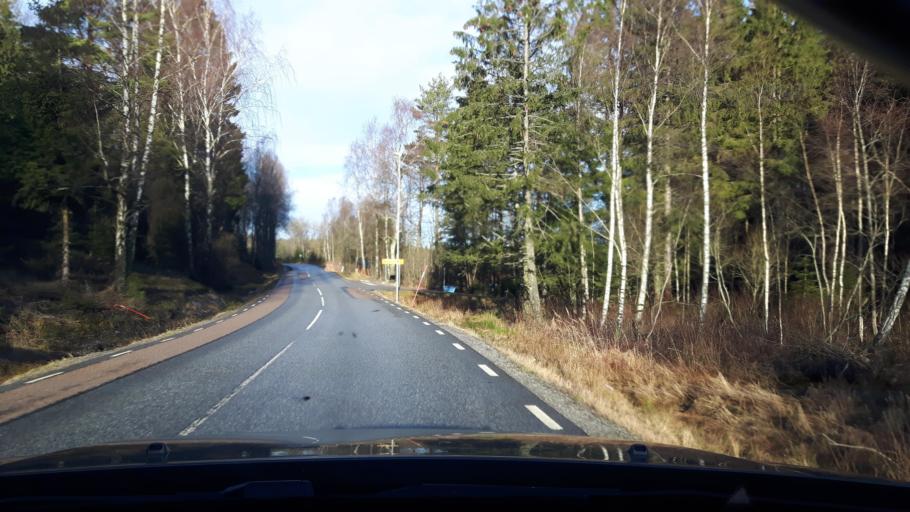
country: SE
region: Vaestra Goetaland
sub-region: Munkedals Kommun
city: Munkedal
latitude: 58.4955
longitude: 11.6939
